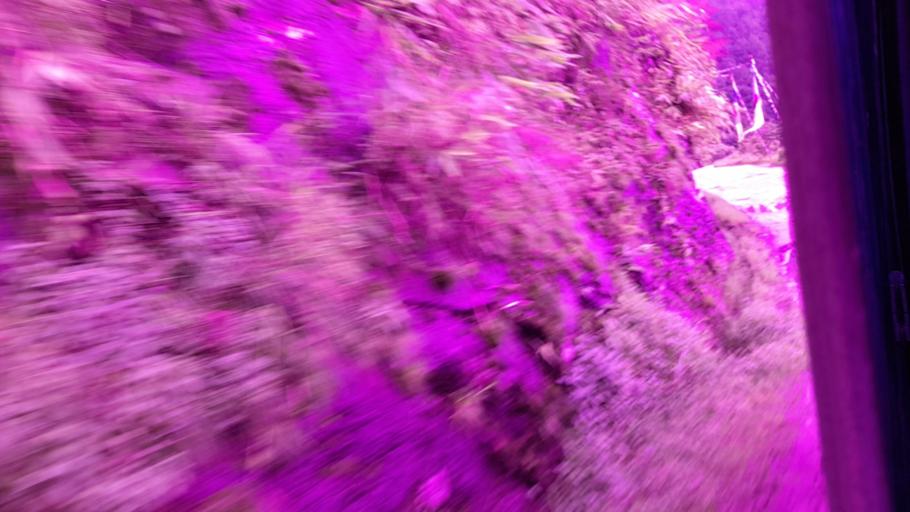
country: NP
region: Central Region
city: Kirtipur
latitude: 27.8306
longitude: 85.2049
